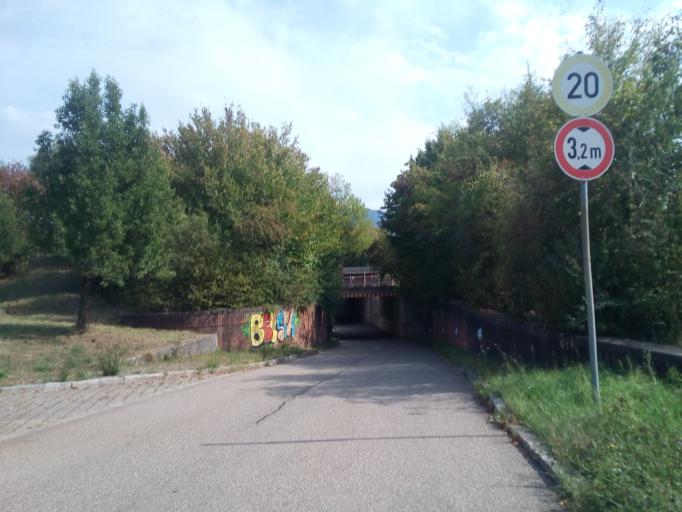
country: DE
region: Baden-Wuerttemberg
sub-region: Freiburg Region
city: Sasbach
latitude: 48.6563
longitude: 8.0888
